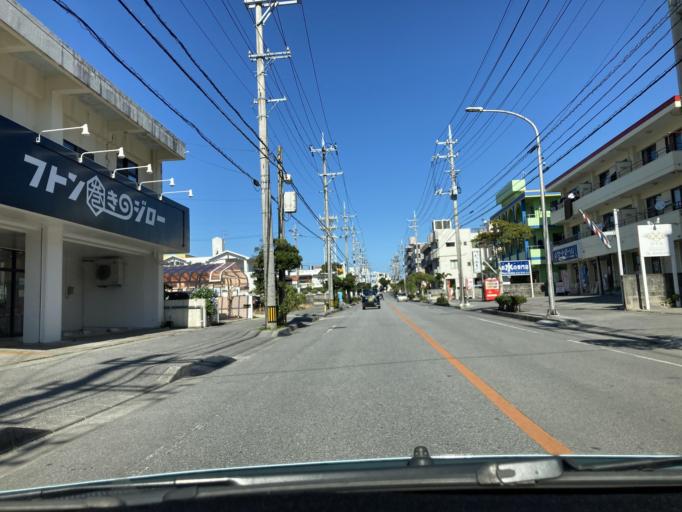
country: JP
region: Okinawa
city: Okinawa
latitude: 26.3228
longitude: 127.8015
